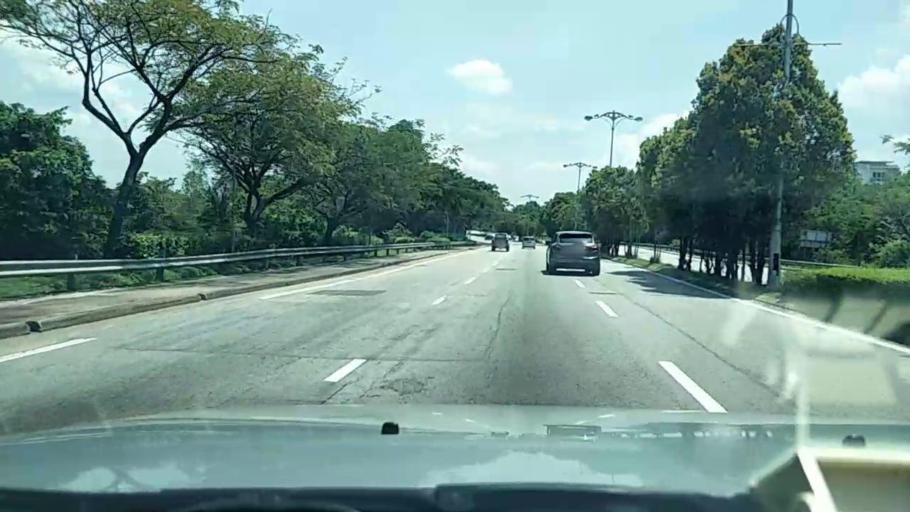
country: MY
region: Putrajaya
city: Putrajaya
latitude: 2.9456
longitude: 101.6702
